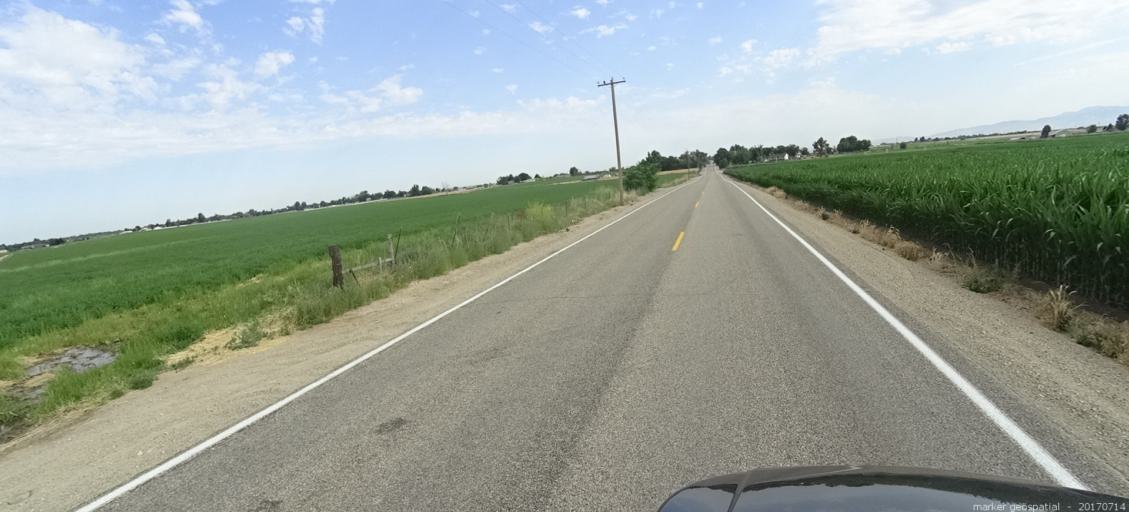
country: US
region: Idaho
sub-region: Ada County
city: Kuna
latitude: 43.4669
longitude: -116.3545
